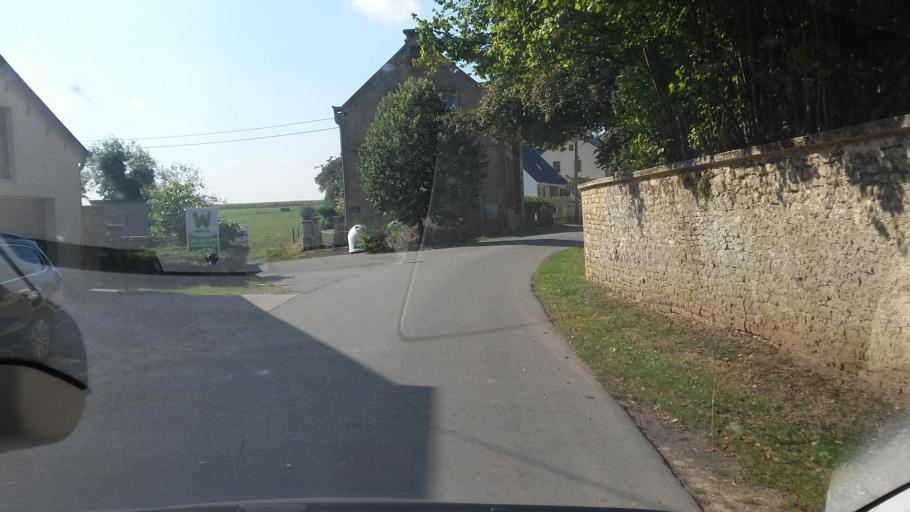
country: LU
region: Diekirch
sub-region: Canton de Redange
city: Beckerich
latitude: 49.7180
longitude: 5.8525
